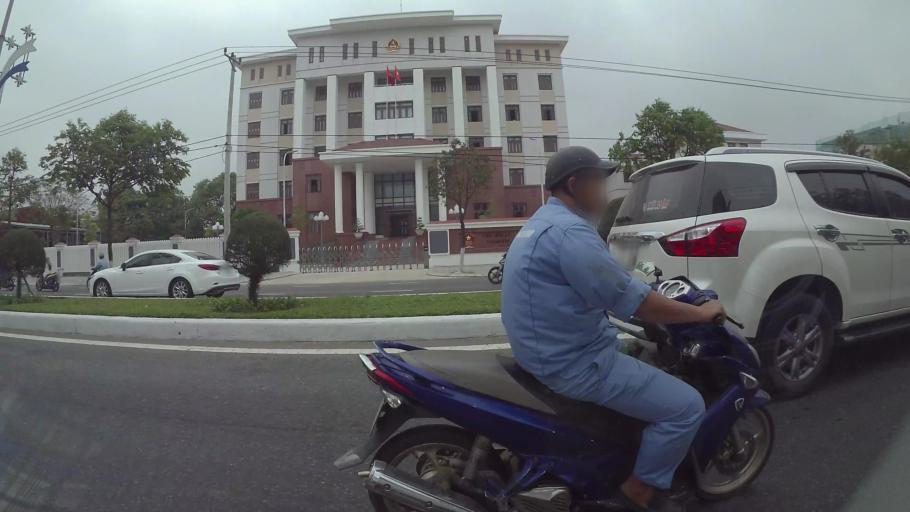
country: VN
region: Da Nang
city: Cam Le
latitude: 16.0272
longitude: 108.2088
